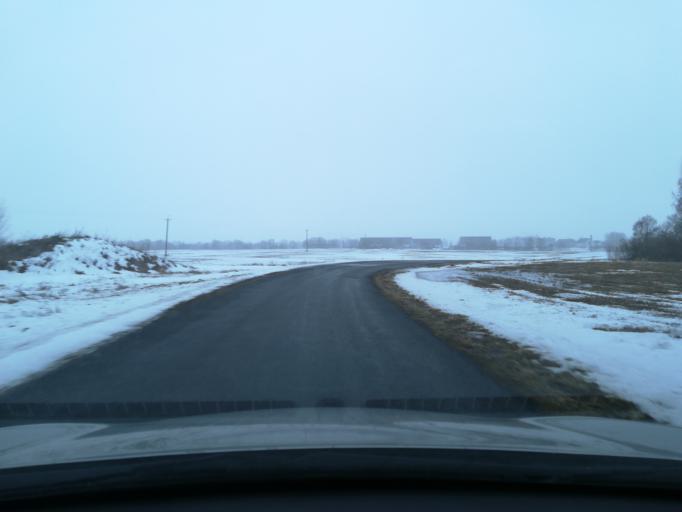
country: EE
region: Harju
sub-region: Raasiku vald
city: Raasiku
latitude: 59.3512
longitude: 25.2069
